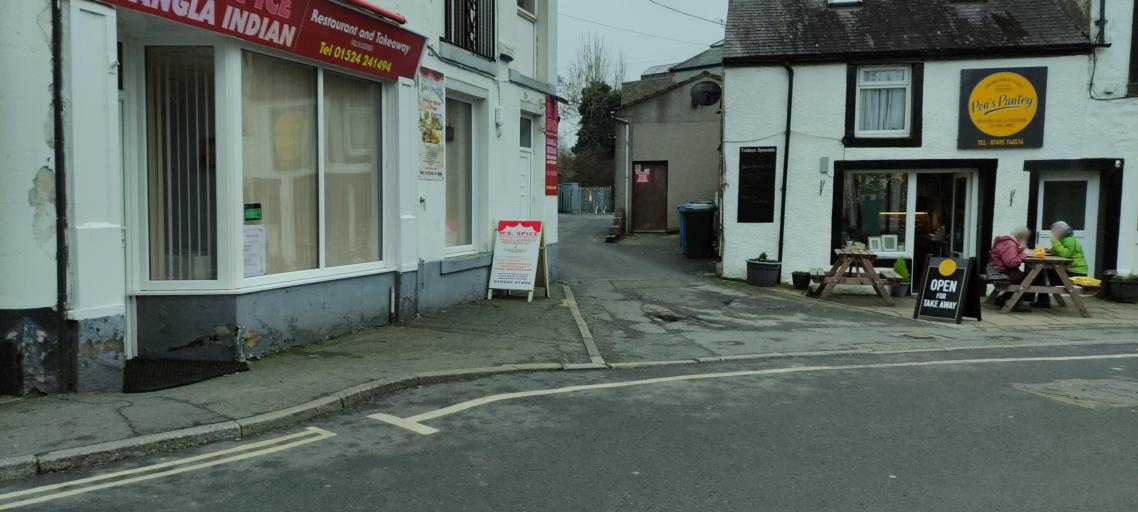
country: GB
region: England
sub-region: North Yorkshire
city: Ingleton
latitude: 54.1540
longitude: -2.4679
